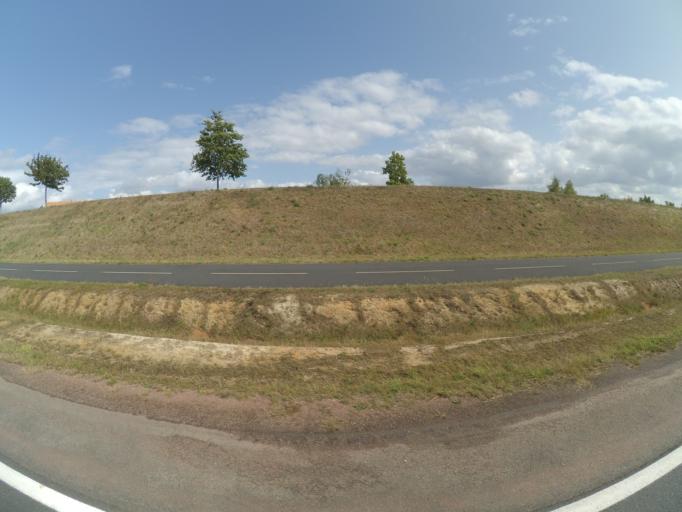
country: FR
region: Pays de la Loire
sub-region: Departement de la Vendee
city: La Bruffiere
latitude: 47.0161
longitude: -1.2052
